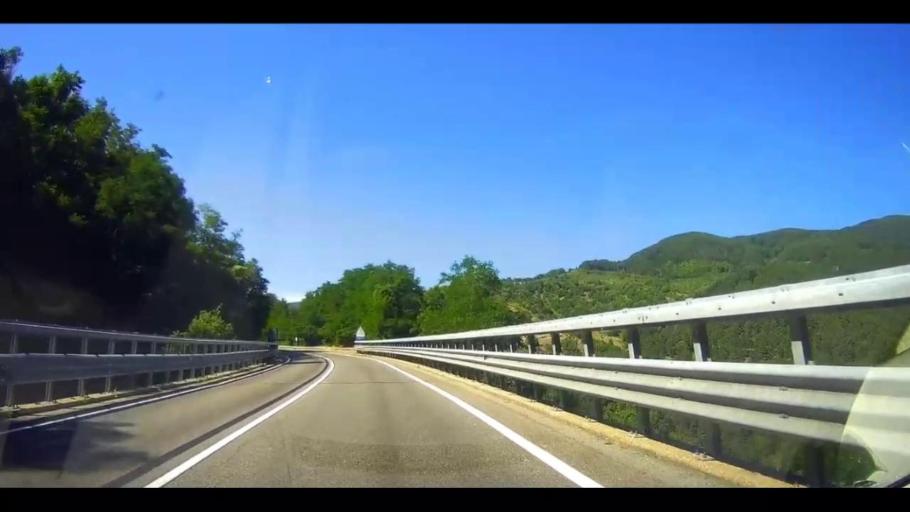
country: IT
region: Calabria
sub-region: Provincia di Cosenza
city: Spezzano Piccolo
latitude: 39.2950
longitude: 16.3545
